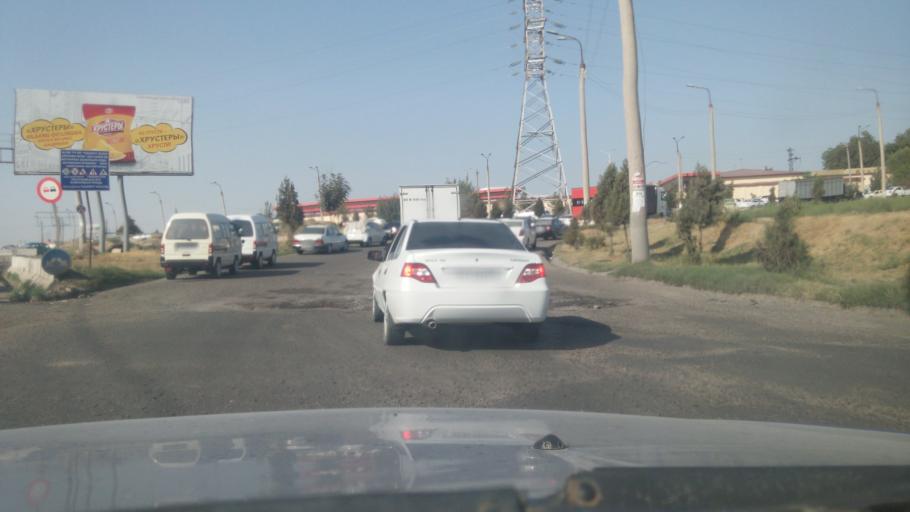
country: UZ
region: Toshkent Shahri
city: Tashkent
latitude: 41.2404
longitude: 69.1673
